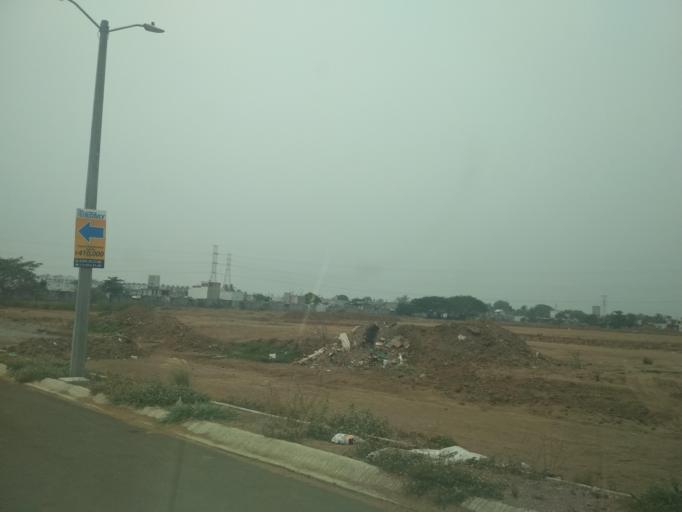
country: MX
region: Veracruz
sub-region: Veracruz
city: Las Amapolas
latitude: 19.1533
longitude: -96.2180
